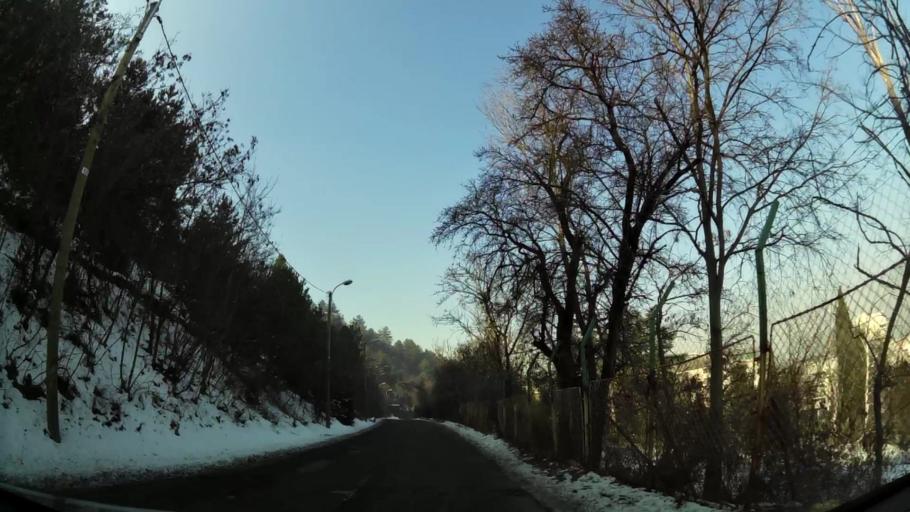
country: MK
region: Karpos
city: Skopje
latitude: 41.9806
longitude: 21.4228
